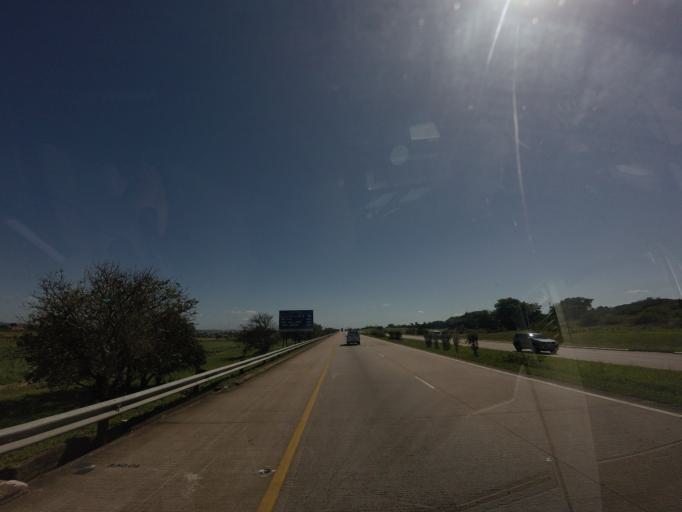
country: ZA
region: KwaZulu-Natal
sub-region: iLembe District Municipality
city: Stanger
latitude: -29.4146
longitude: 31.2778
